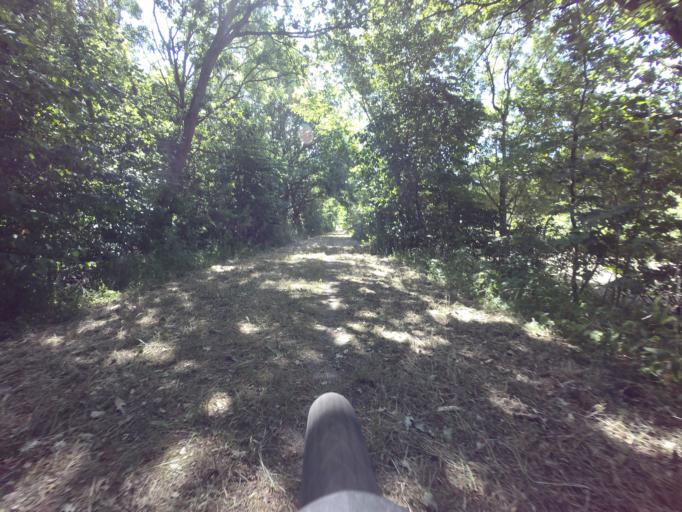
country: DK
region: Central Jutland
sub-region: Odder Kommune
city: Odder
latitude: 55.9224
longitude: 10.1089
